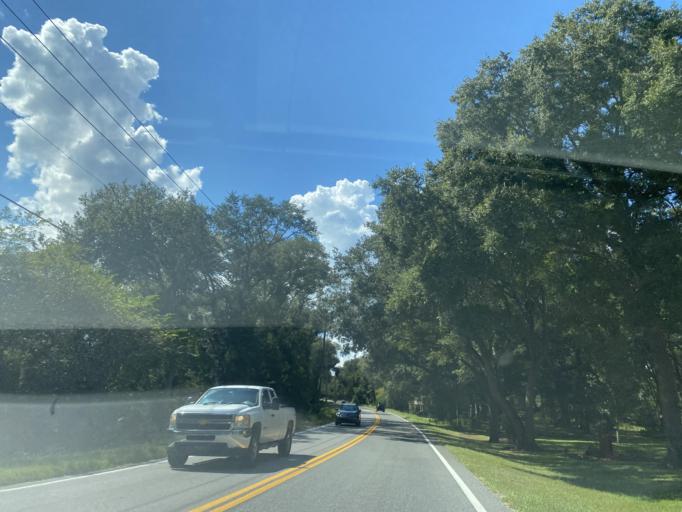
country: US
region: Florida
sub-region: Lake County
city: Lady Lake
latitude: 28.9835
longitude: -81.9005
